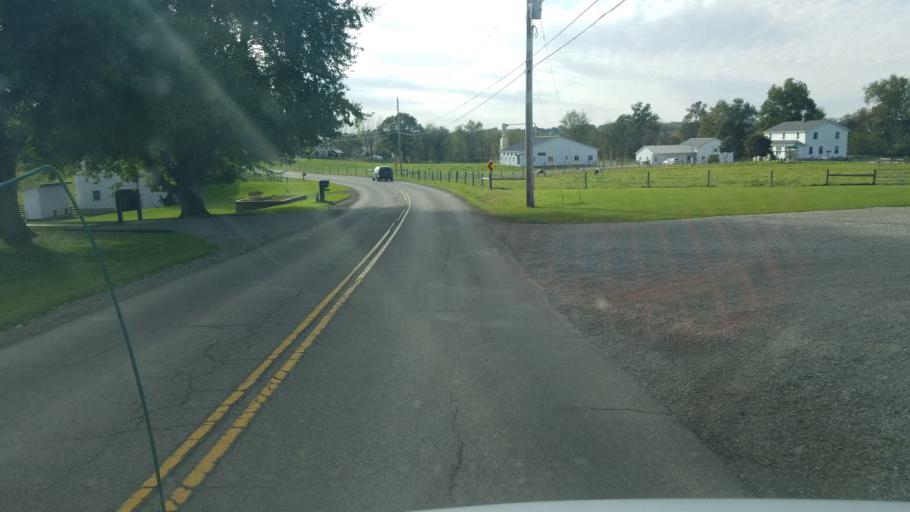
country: US
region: Ohio
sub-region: Wayne County
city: Apple Creek
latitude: 40.6868
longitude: -81.8533
